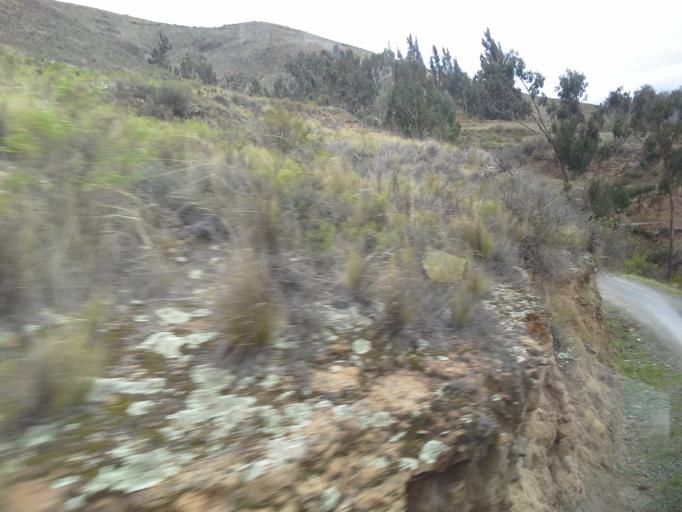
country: BO
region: Cochabamba
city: Colomi
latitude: -17.4118
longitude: -65.8075
